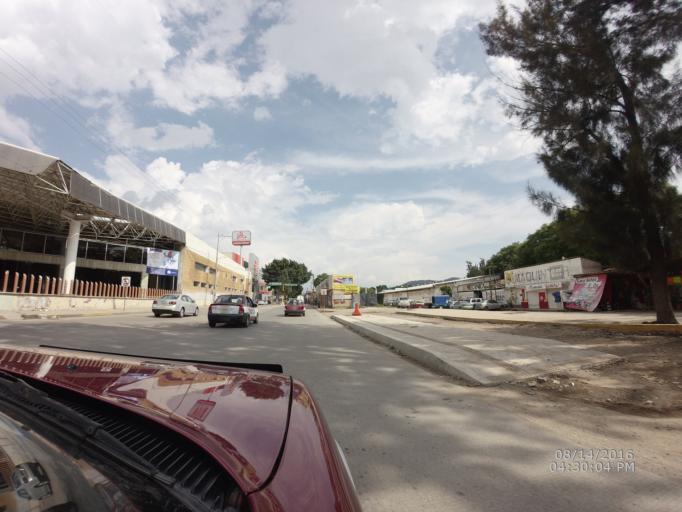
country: MX
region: Oaxaca
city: Oaxaca de Juarez
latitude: 17.0794
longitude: -96.7431
